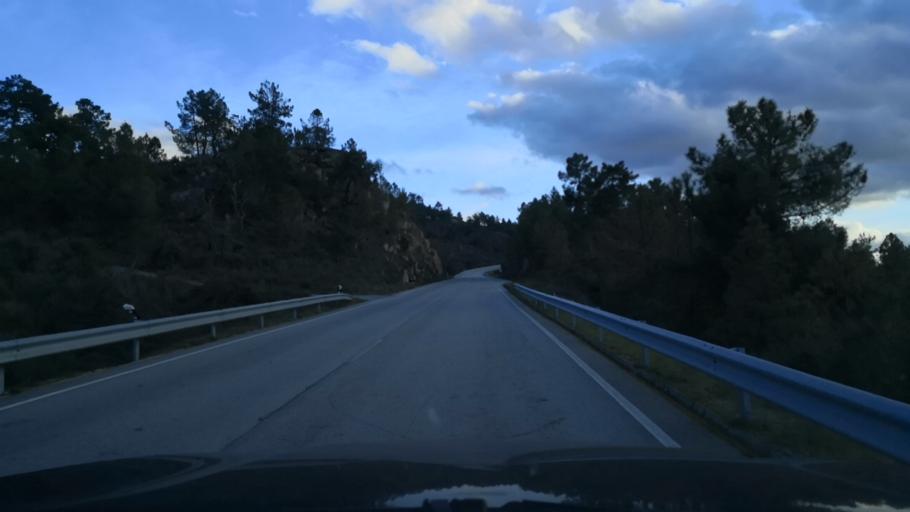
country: PT
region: Braganca
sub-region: Carrazeda de Ansiaes
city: Carrazeda de Anciaes
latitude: 41.2901
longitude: -7.3369
